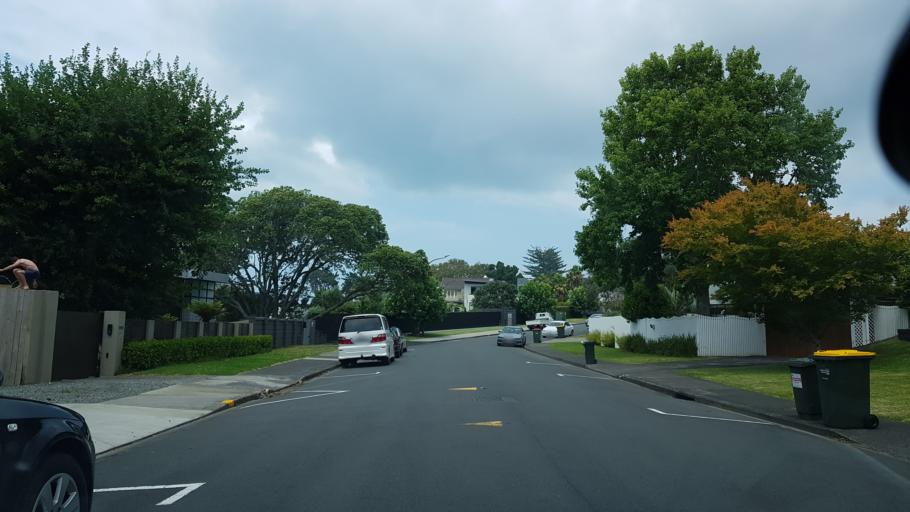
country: NZ
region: Auckland
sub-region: Auckland
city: North Shore
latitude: -36.7971
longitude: 174.7845
